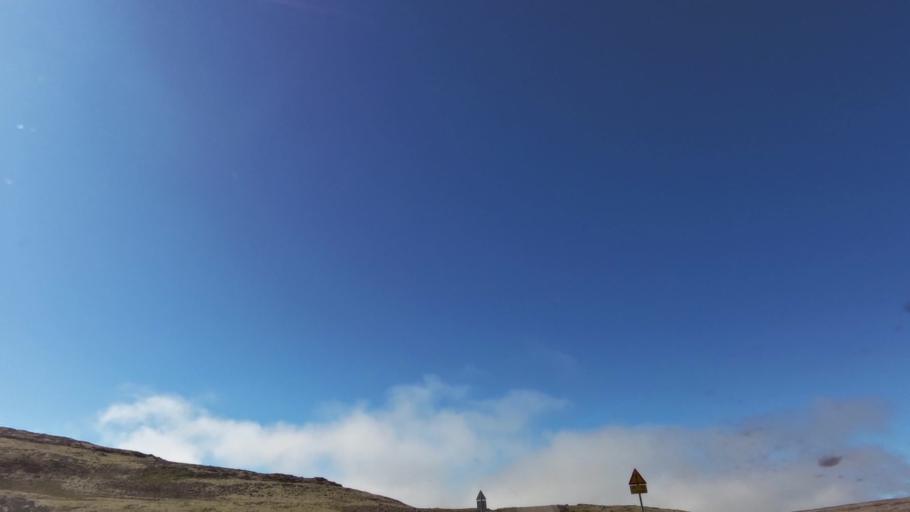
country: IS
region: West
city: Olafsvik
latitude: 65.5515
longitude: -24.2177
